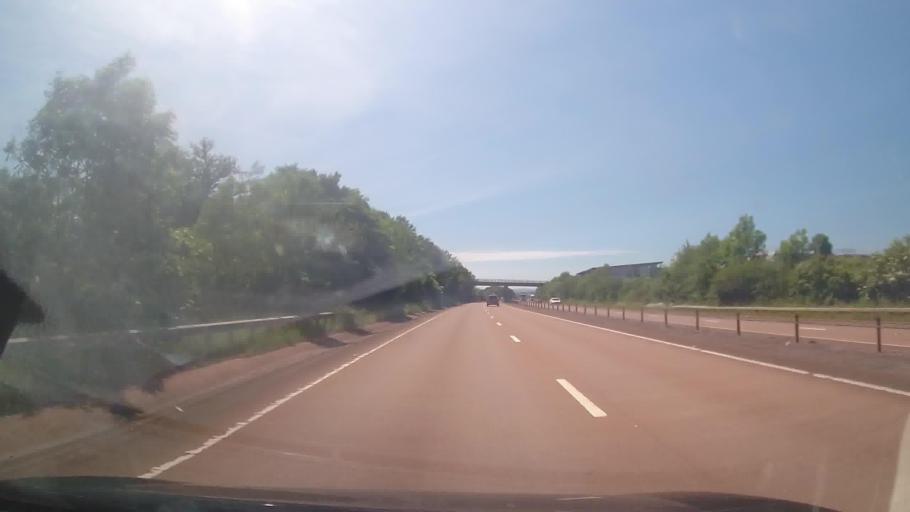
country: GB
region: England
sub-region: Devon
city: Topsham
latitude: 50.7284
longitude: -3.4078
